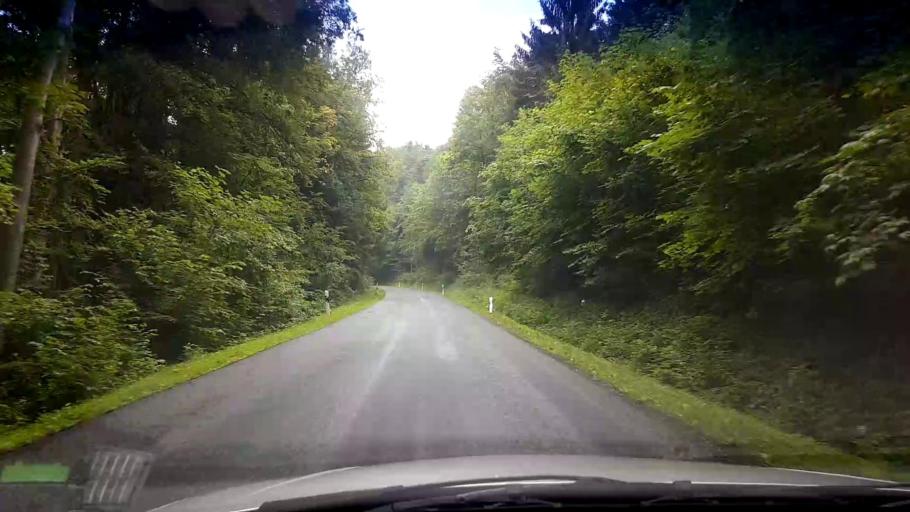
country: DE
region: Bavaria
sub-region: Upper Franconia
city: Wattendorf
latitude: 50.0602
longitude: 11.0871
